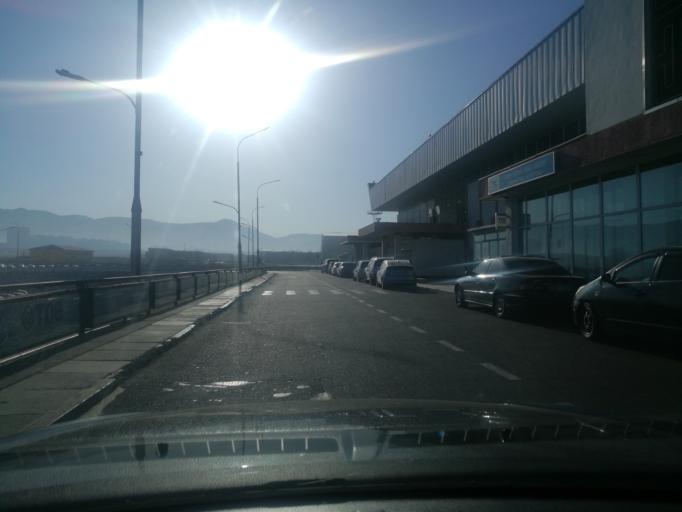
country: MN
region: Ulaanbaatar
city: Ulaanbaatar
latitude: 47.8528
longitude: 106.7631
